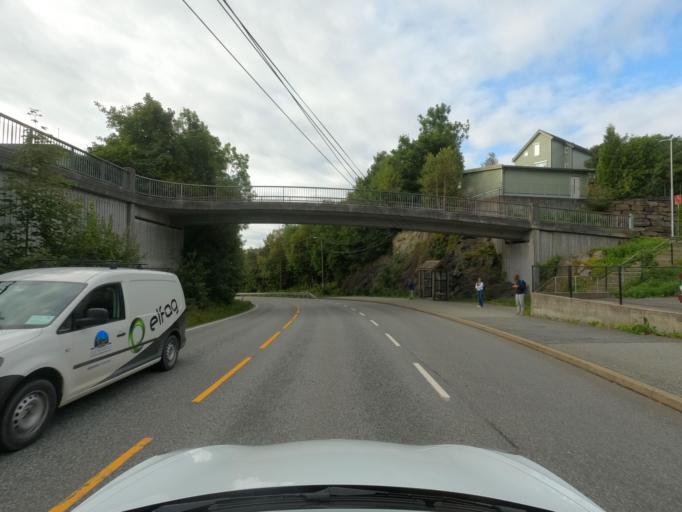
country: NO
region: Hordaland
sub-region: Bergen
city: Sandsli
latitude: 60.3128
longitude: 5.2899
